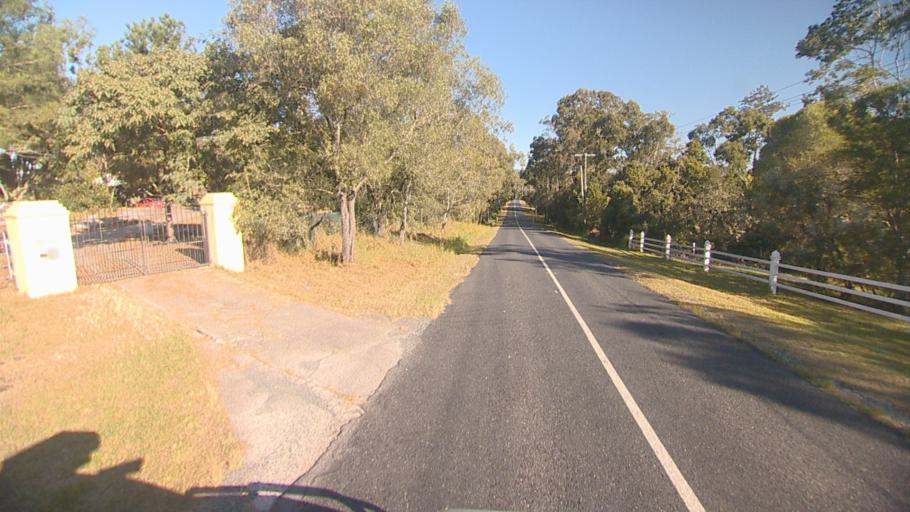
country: AU
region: Queensland
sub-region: Logan
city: Logan Reserve
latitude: -27.7316
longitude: 153.1043
